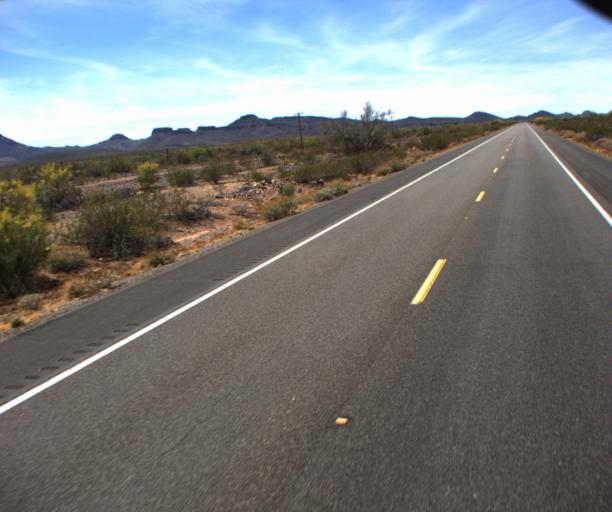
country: US
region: Arizona
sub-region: La Paz County
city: Quartzsite
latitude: 33.6691
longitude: -113.9882
